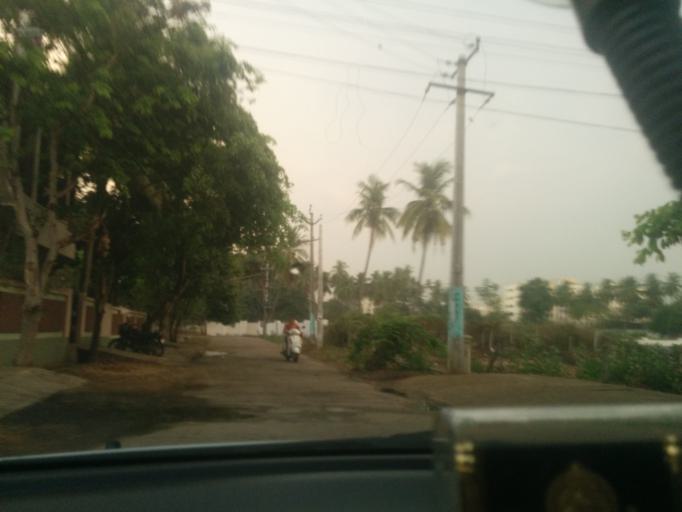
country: IN
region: Andhra Pradesh
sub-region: East Godavari
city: Rajahmundry
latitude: 17.0235
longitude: 81.7950
